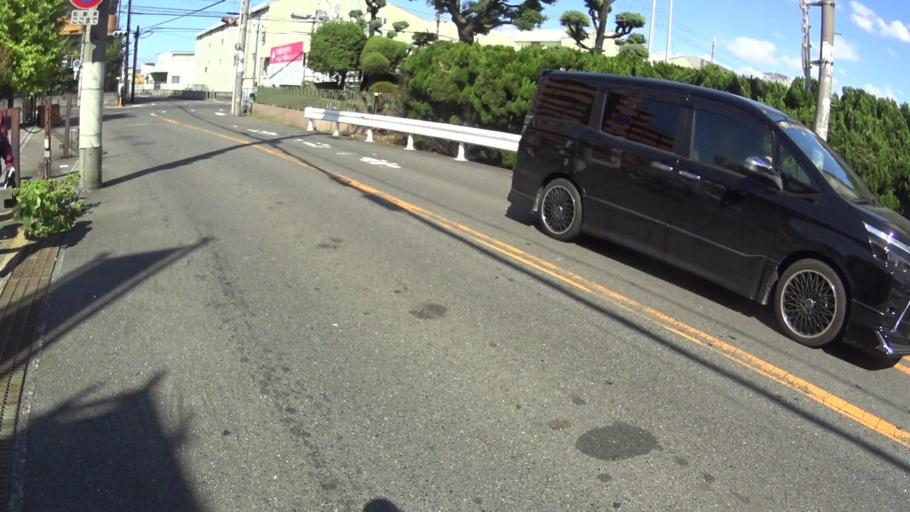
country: JP
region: Ehime
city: Kihoku-cho
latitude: 33.3868
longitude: 132.8354
